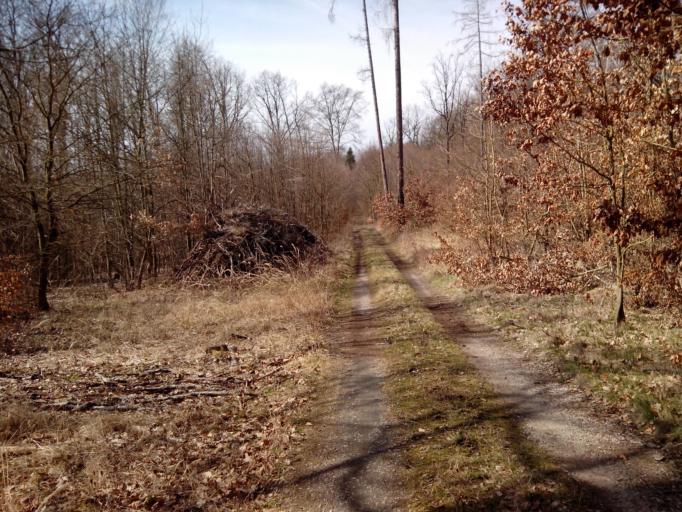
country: CZ
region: Central Bohemia
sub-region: Okres Beroun
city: Beroun
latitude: 49.9354
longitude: 14.1085
